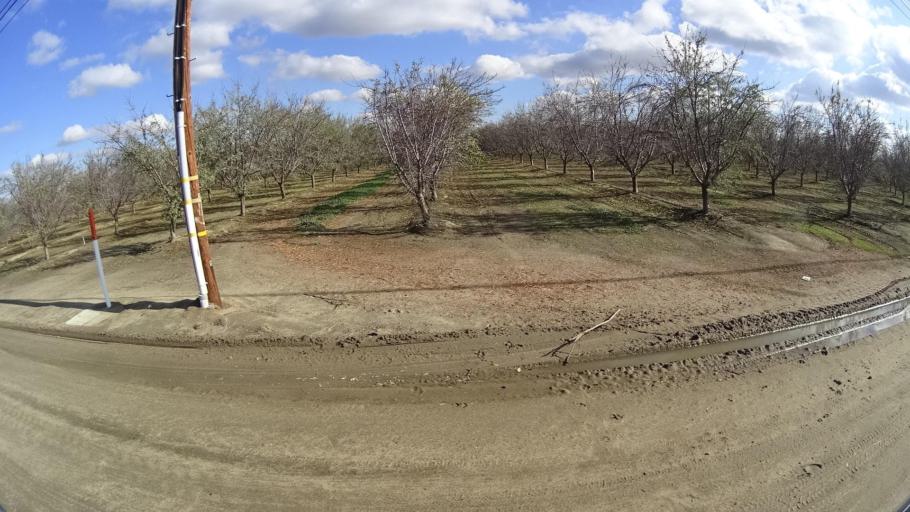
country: US
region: California
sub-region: Kern County
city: McFarland
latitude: 35.7014
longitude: -119.2408
